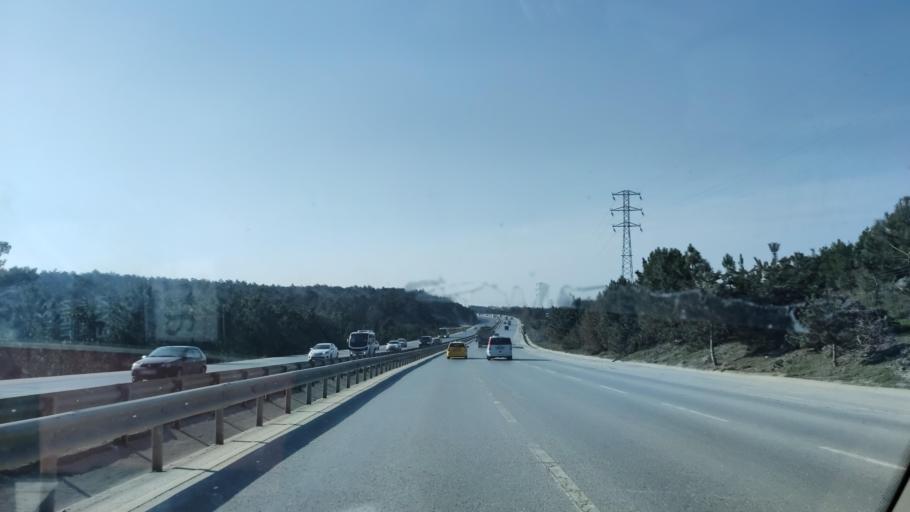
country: TR
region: Istanbul
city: Basaksehir
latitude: 41.1641
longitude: 28.7698
